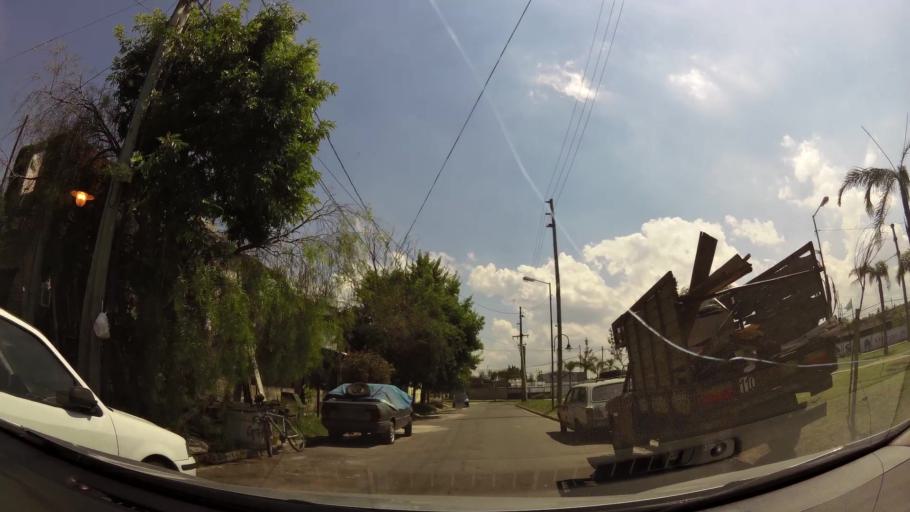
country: AR
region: Buenos Aires
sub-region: Partido de Tigre
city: Tigre
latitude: -34.4682
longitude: -58.5956
